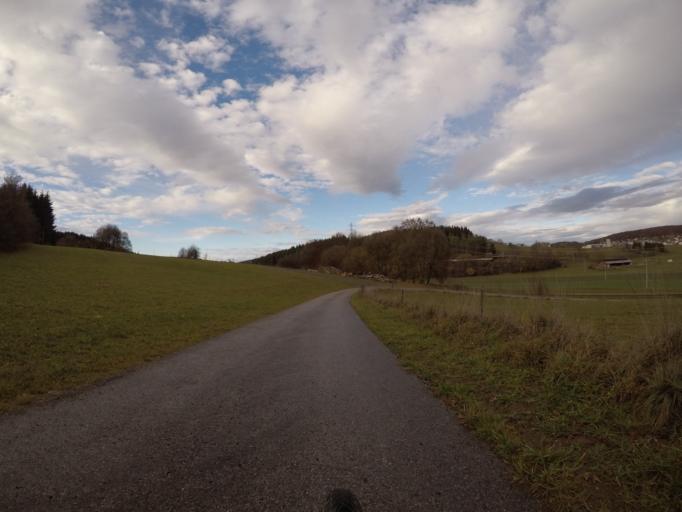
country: DE
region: Baden-Wuerttemberg
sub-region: Tuebingen Region
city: Sankt Johann
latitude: 48.4450
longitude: 9.3326
